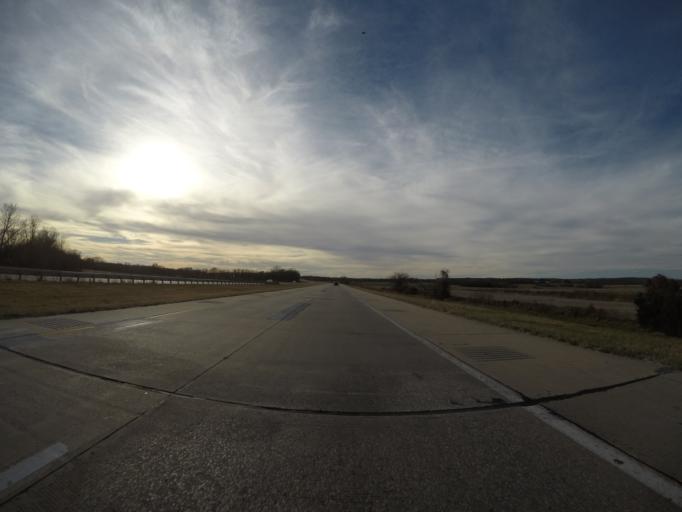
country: US
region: Kansas
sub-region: Franklin County
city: Ottawa
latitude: 38.5568
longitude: -95.3379
